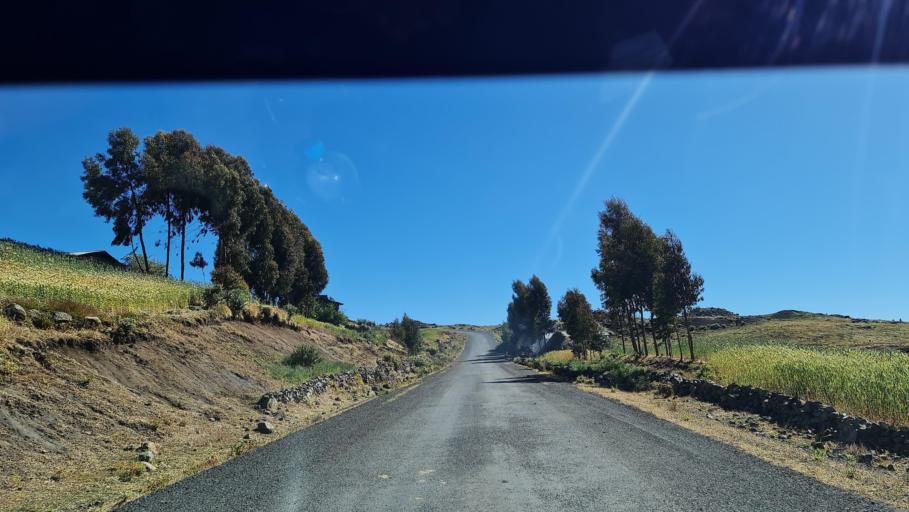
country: ET
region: Amhara
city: Debark'
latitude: 13.1342
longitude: 38.1731
